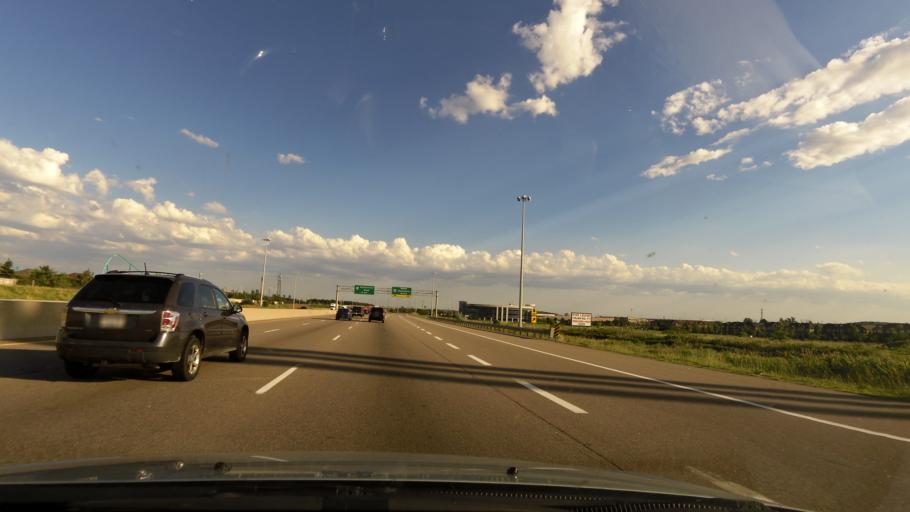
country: CA
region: Ontario
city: Vaughan
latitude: 43.8543
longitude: -79.5504
